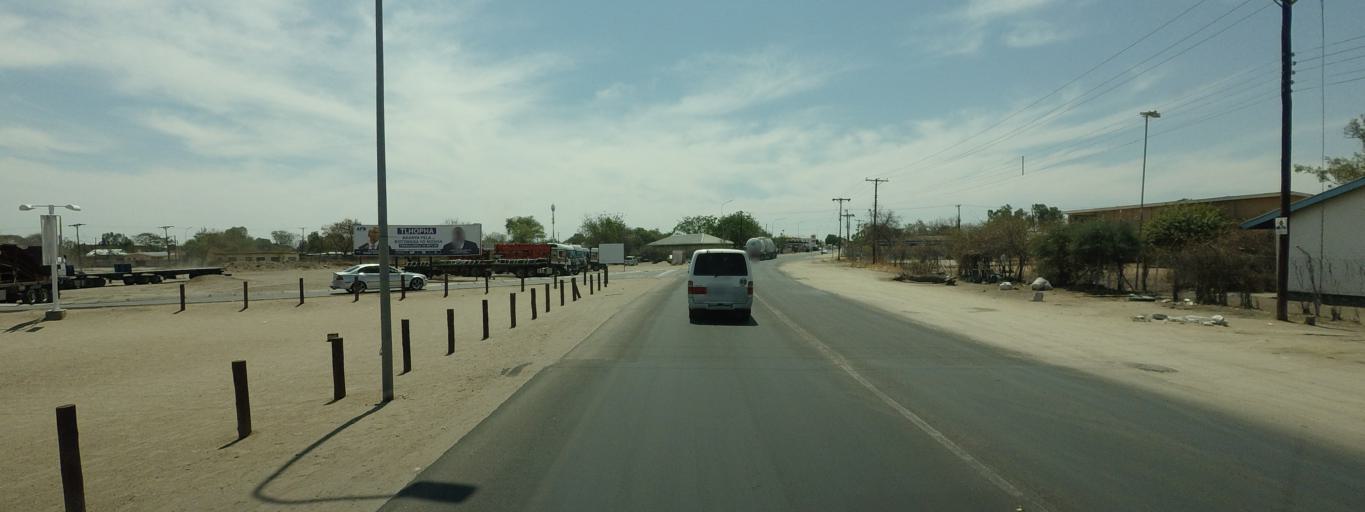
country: BW
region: North East
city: Francistown
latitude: -21.1695
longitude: 27.4963
